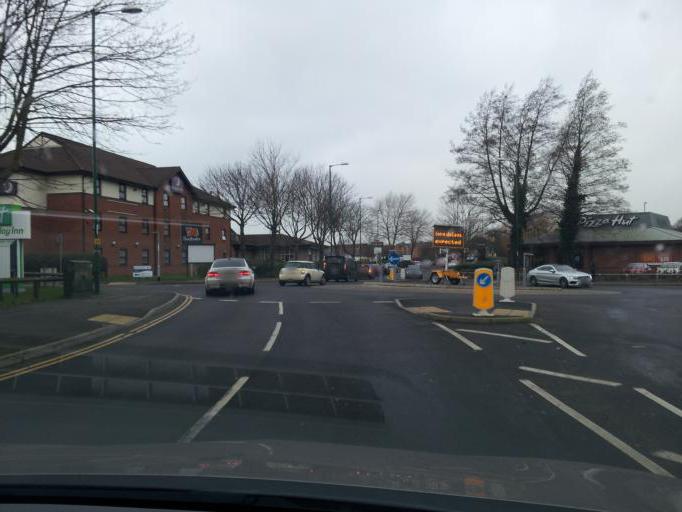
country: GB
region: England
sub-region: Nottingham
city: Nottingham
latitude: 52.9451
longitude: -1.1647
